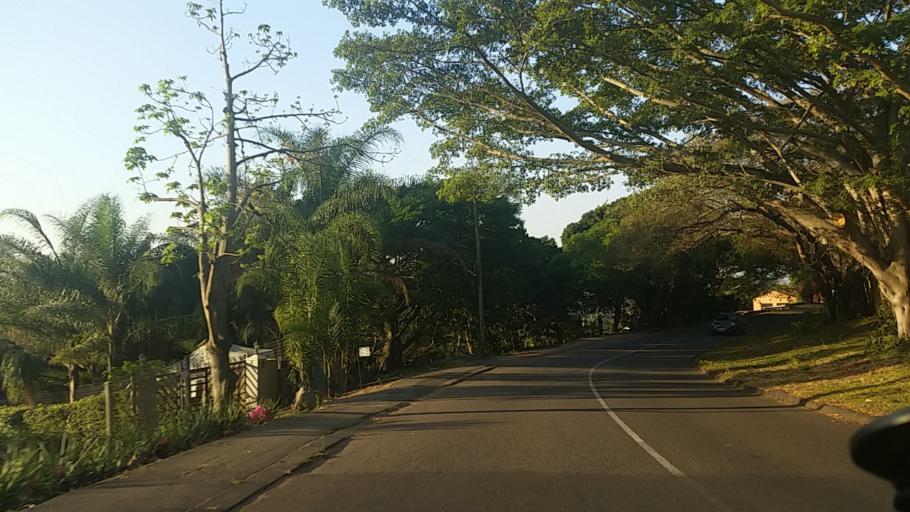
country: ZA
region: KwaZulu-Natal
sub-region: eThekwini Metropolitan Municipality
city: Berea
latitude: -29.8537
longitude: 30.9116
